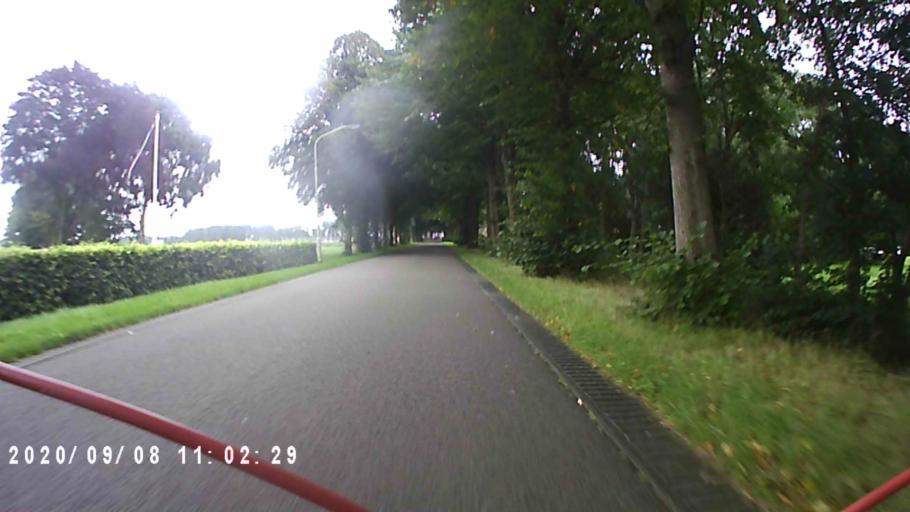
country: NL
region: Groningen
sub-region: Gemeente Haren
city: Haren
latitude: 53.1967
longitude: 6.6698
